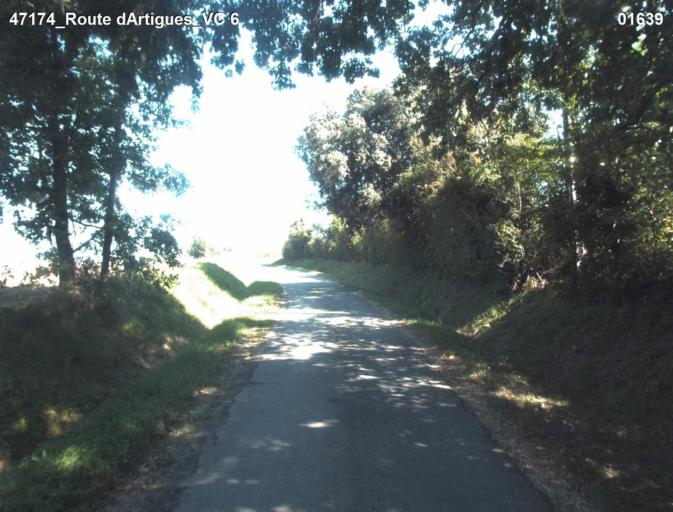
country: FR
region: Midi-Pyrenees
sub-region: Departement du Gers
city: Condom
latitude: 44.0216
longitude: 0.3345
